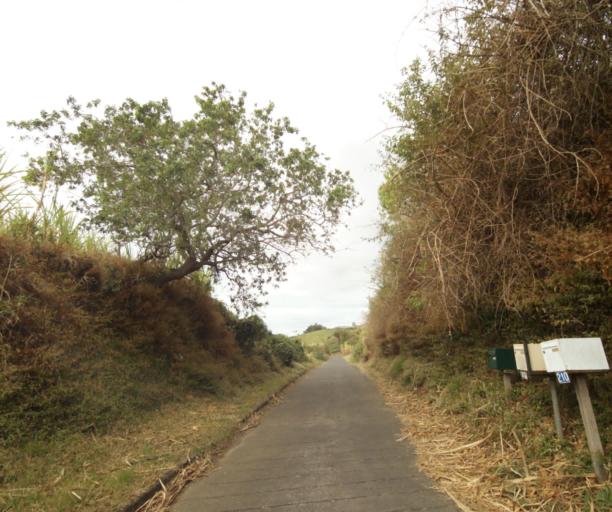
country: RE
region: Reunion
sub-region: Reunion
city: Saint-Paul
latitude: -21.0292
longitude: 55.3171
